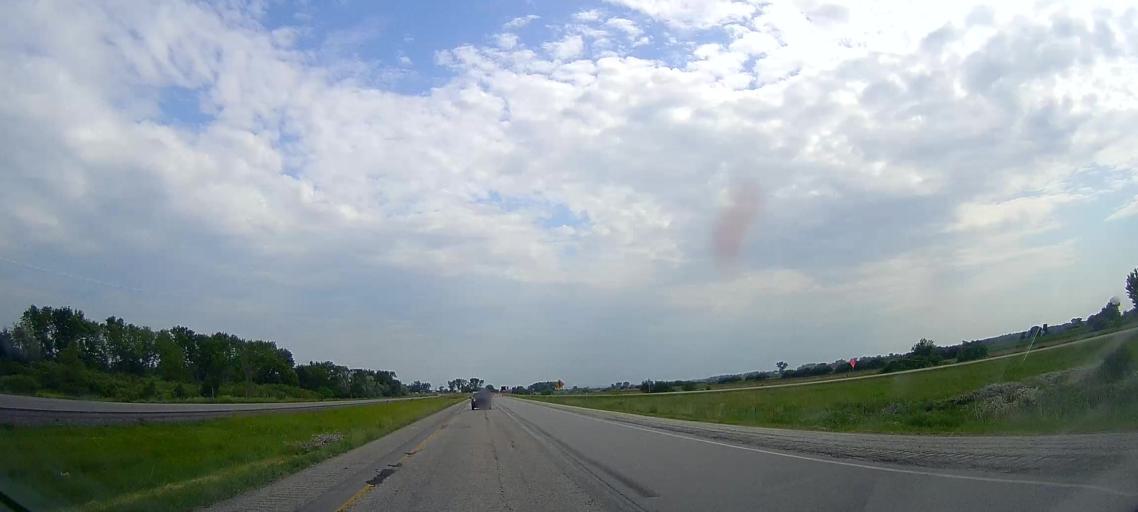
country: US
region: Nebraska
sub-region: Burt County
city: Tekamah
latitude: 41.7407
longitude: -96.0480
